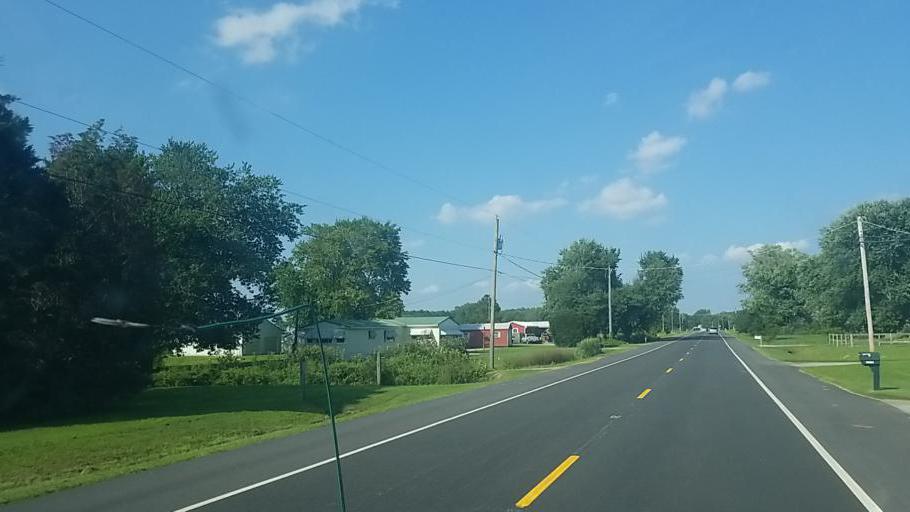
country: US
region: Maryland
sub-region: Worcester County
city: Berlin
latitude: 38.3607
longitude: -75.2084
